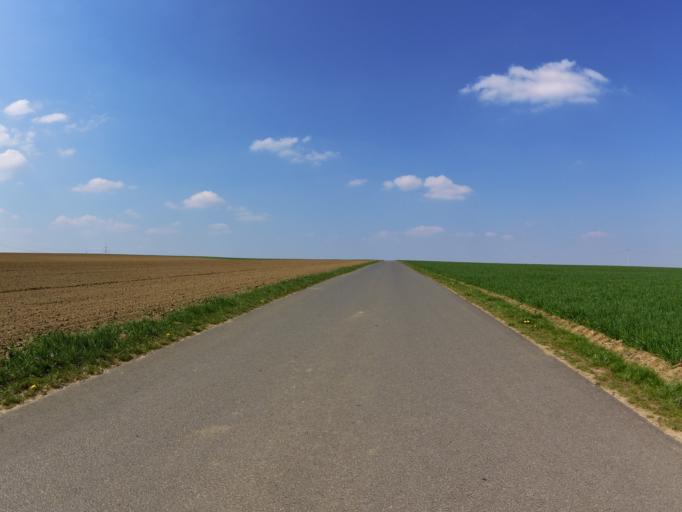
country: DE
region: Bavaria
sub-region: Regierungsbezirk Unterfranken
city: Biebelried
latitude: 49.7613
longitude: 10.0682
